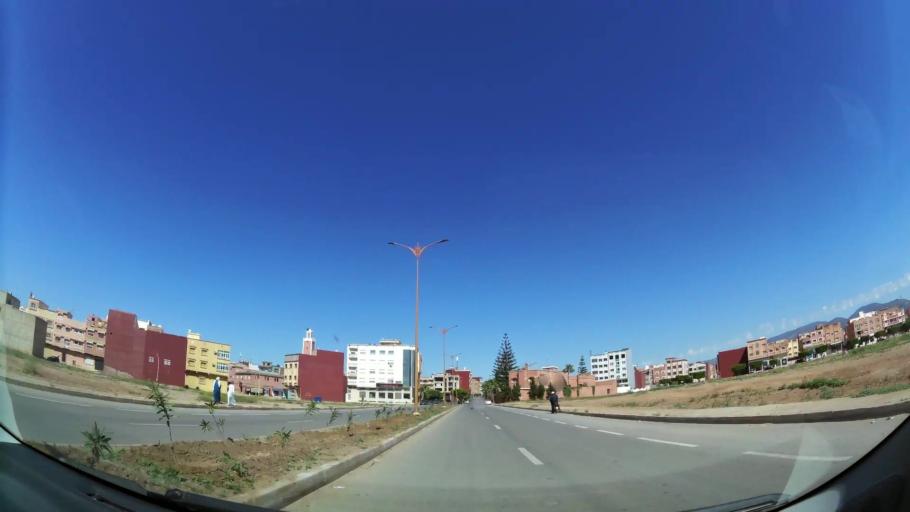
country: MA
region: Oriental
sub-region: Berkane-Taourirt
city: Berkane
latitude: 34.9344
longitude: -2.3274
